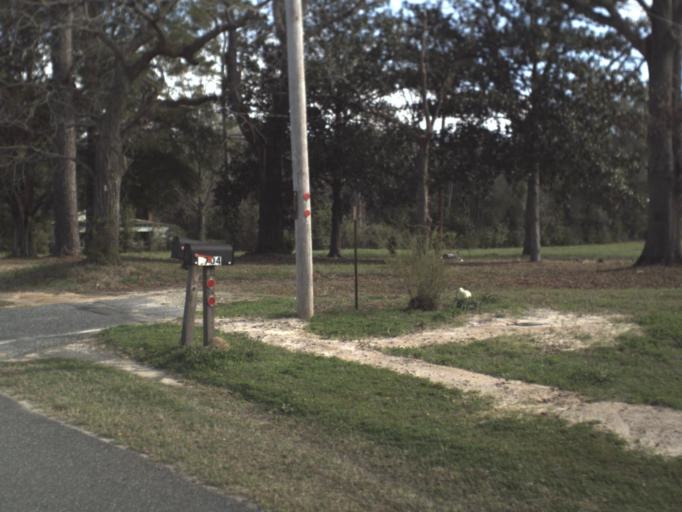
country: US
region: Florida
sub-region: Jackson County
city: Marianna
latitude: 30.8340
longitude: -85.1669
